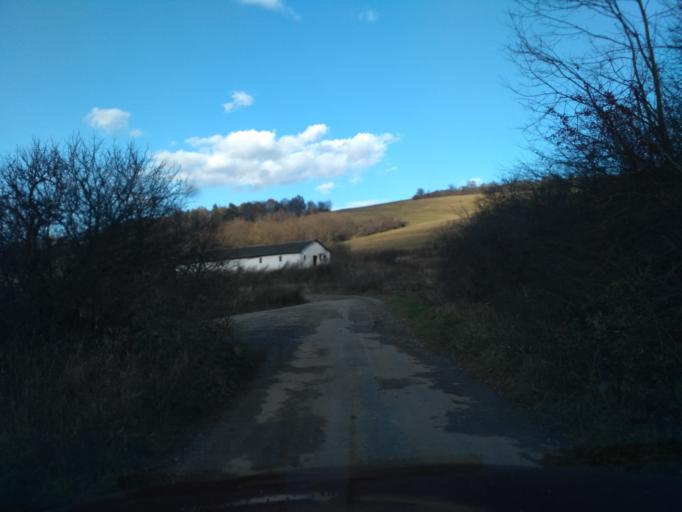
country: SK
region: Presovsky
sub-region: Okres Presov
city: Presov
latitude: 48.9293
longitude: 21.1941
